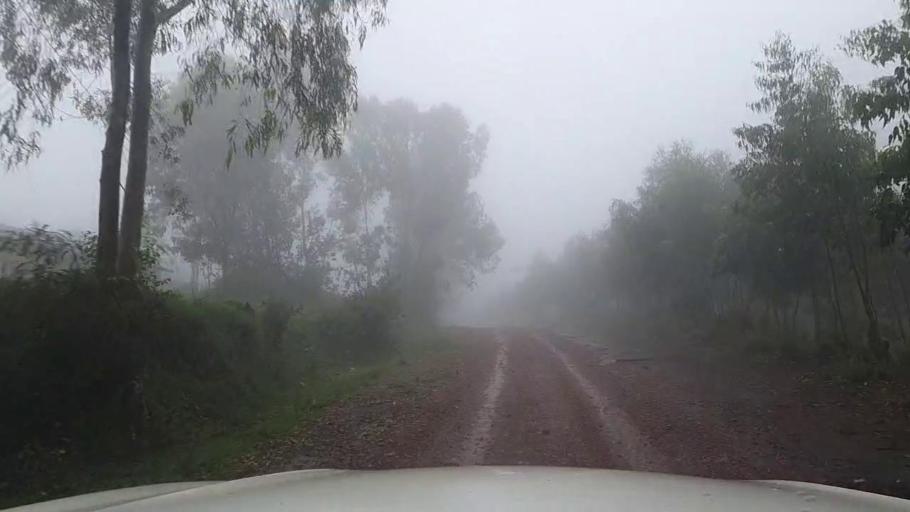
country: RW
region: Kigali
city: Kigali
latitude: -1.7707
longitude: 29.9980
